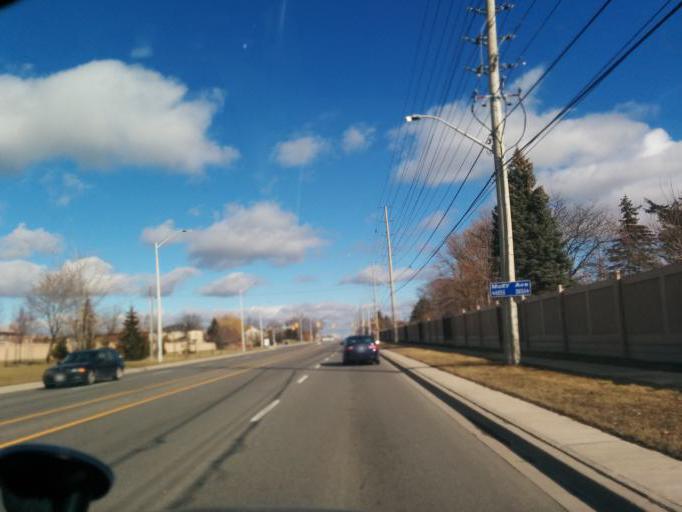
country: CA
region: Ontario
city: Mississauga
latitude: 43.6039
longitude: -79.6229
